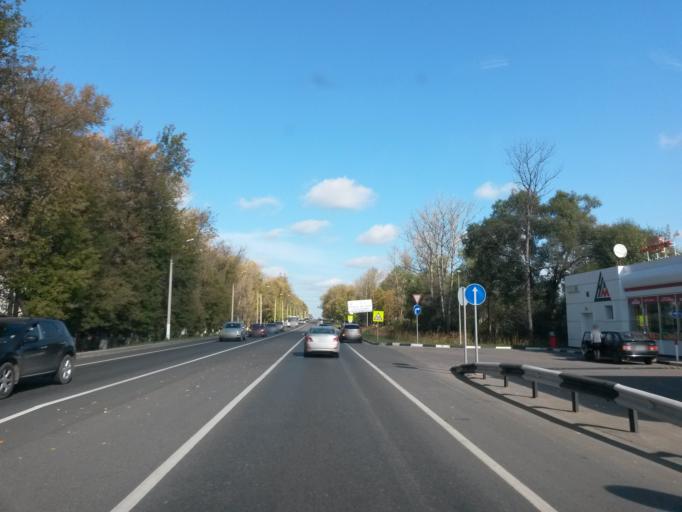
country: RU
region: Moskovskaya
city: L'vovskiy
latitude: 55.3163
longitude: 37.5287
